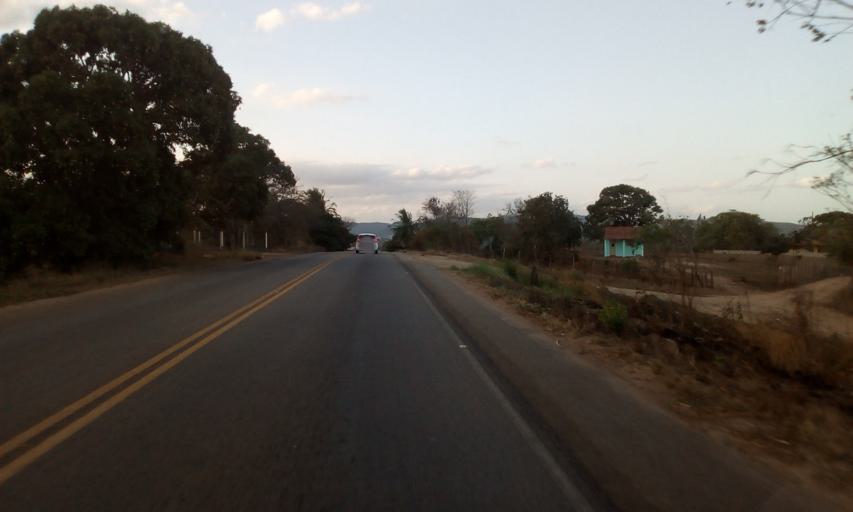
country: BR
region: Paraiba
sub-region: Guarabira
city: Guarabira
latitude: -6.8970
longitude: -35.4620
